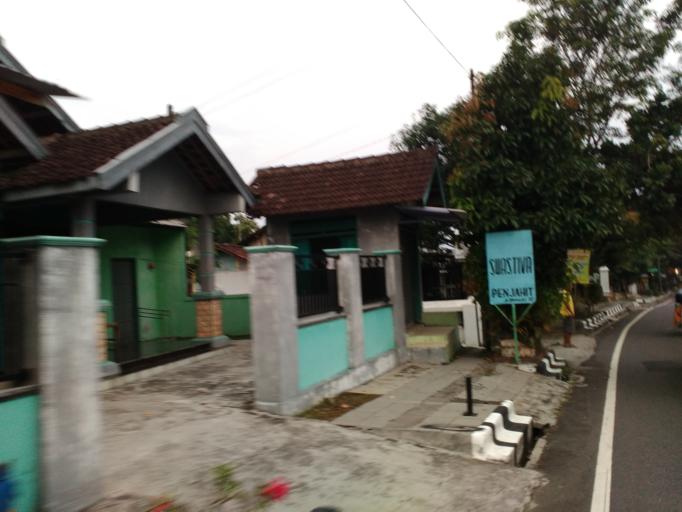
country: ID
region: Central Java
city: Boyolali
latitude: -7.5348
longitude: 110.6034
